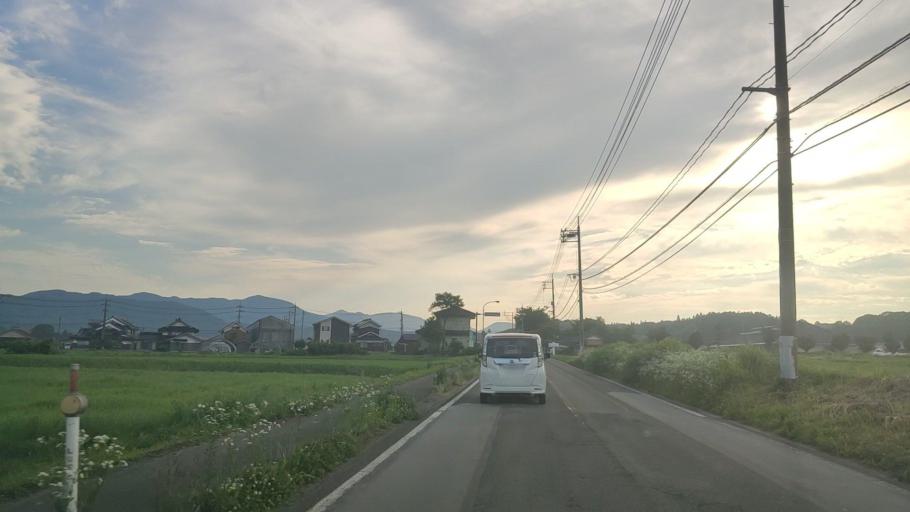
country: JP
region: Tottori
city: Kurayoshi
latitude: 35.2821
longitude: 133.6907
